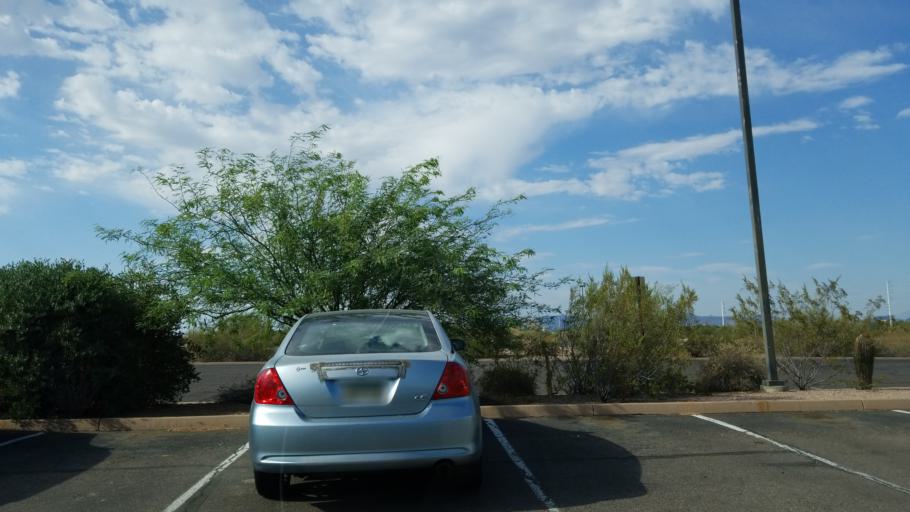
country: US
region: Arizona
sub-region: Maricopa County
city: Tempe Junction
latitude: 33.4620
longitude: -111.9433
